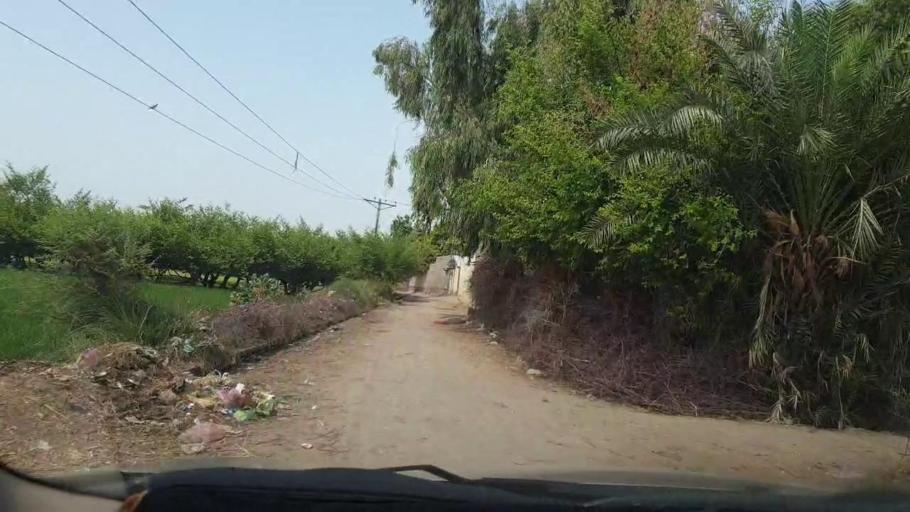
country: PK
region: Sindh
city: Larkana
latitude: 27.5869
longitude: 68.1453
